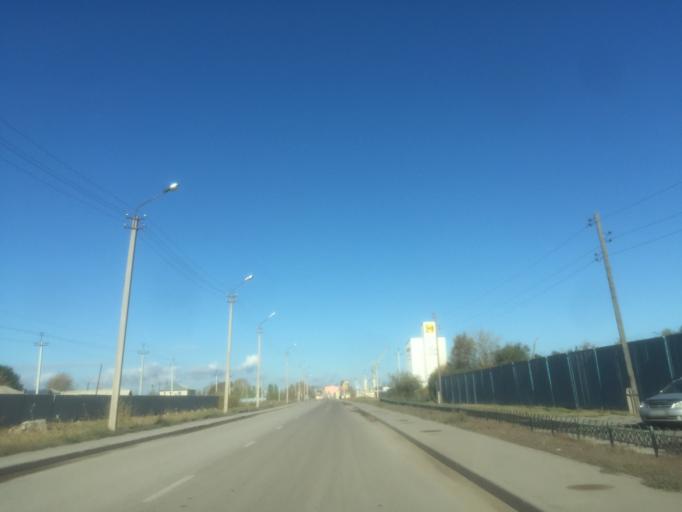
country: KZ
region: Astana Qalasy
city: Astana
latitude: 51.2027
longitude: 71.3627
